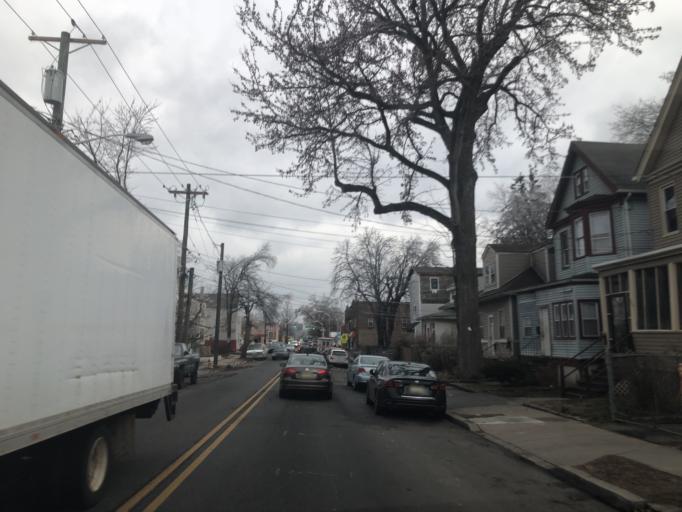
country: US
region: New Jersey
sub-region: Essex County
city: Irvington
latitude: 40.7509
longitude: -74.2305
